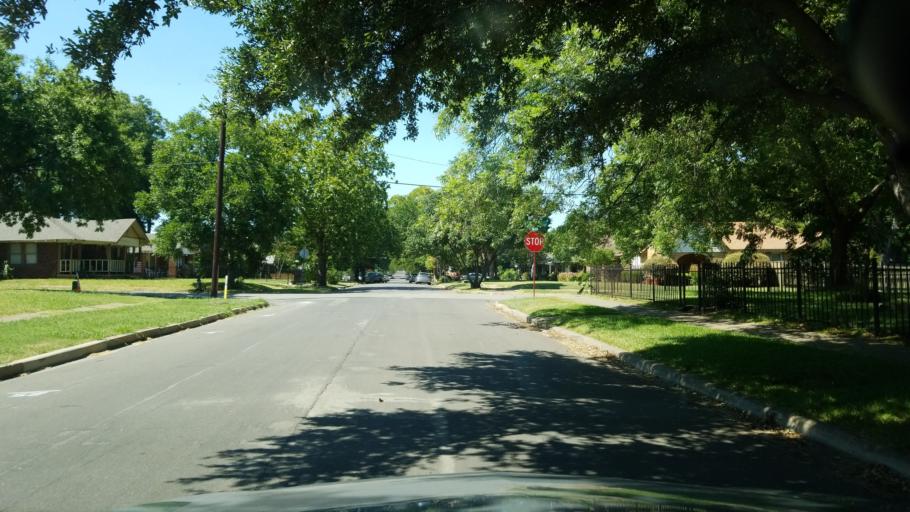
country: US
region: Texas
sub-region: Dallas County
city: Cockrell Hill
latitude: 32.7329
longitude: -96.8555
